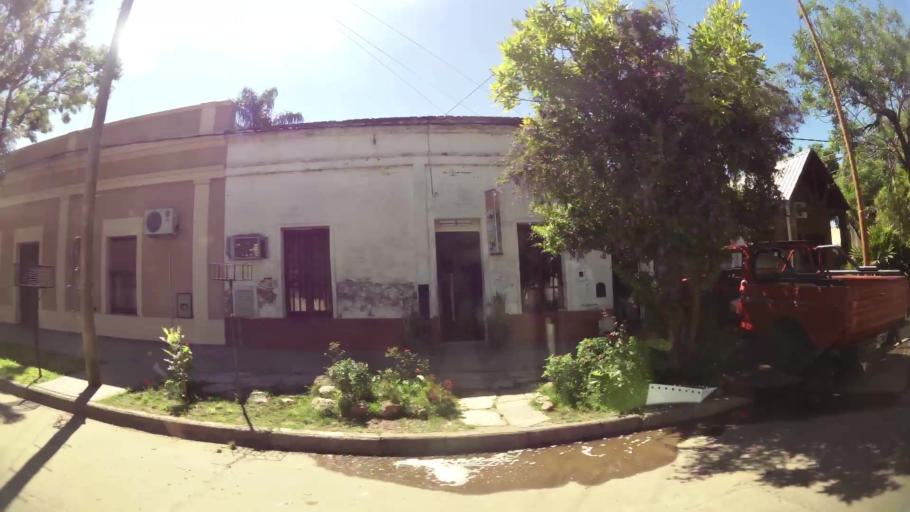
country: AR
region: Santa Fe
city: Esperanza
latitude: -31.4412
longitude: -60.9270
